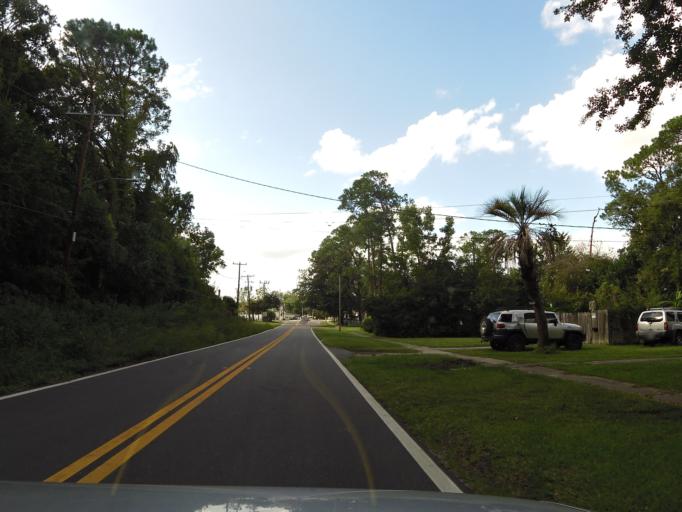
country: US
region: Florida
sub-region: Duval County
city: Jacksonville
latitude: 30.2733
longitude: -81.7305
